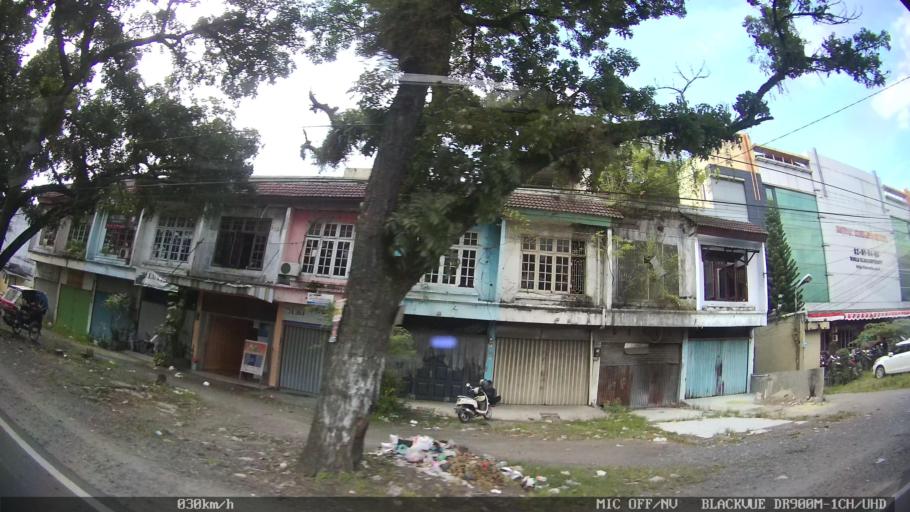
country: ID
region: North Sumatra
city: Medan
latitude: 3.6154
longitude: 98.6491
